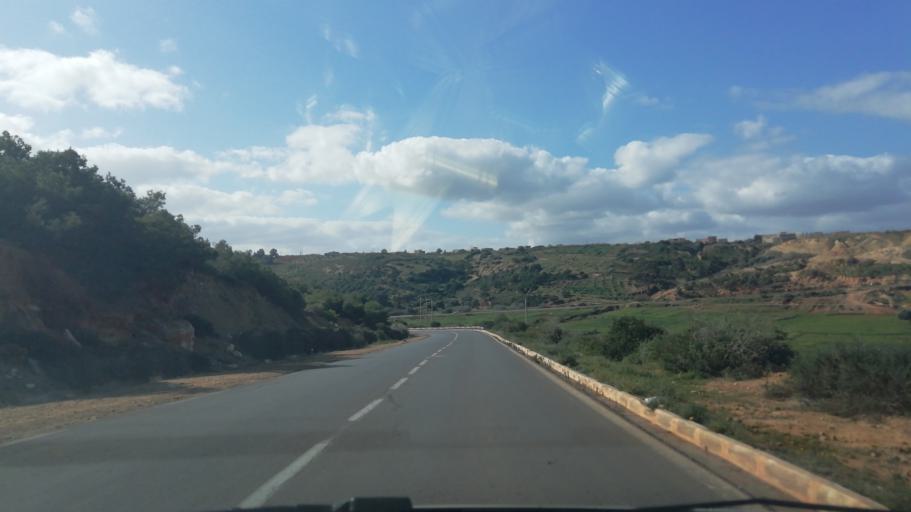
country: DZ
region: Relizane
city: Mazouna
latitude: 36.3206
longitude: 0.6851
